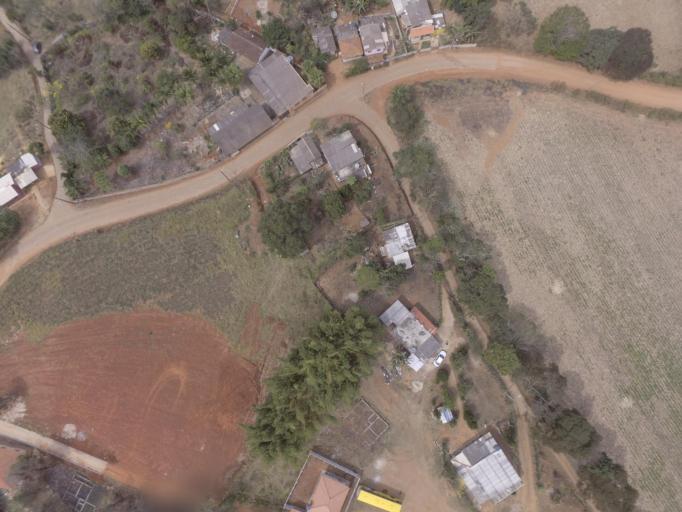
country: BR
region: Minas Gerais
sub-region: Tiradentes
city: Tiradentes
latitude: -21.0572
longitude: -44.0695
